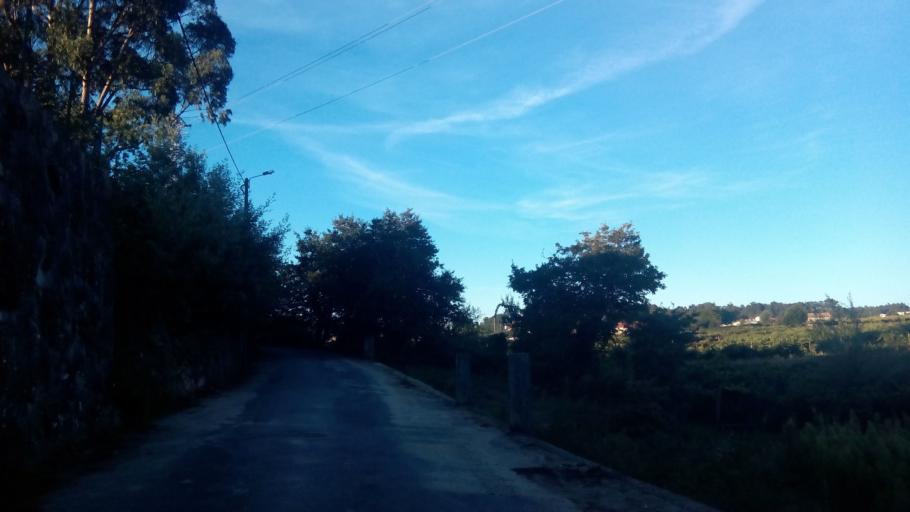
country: PT
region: Porto
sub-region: Paredes
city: Baltar
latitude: 41.1858
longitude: -8.3772
